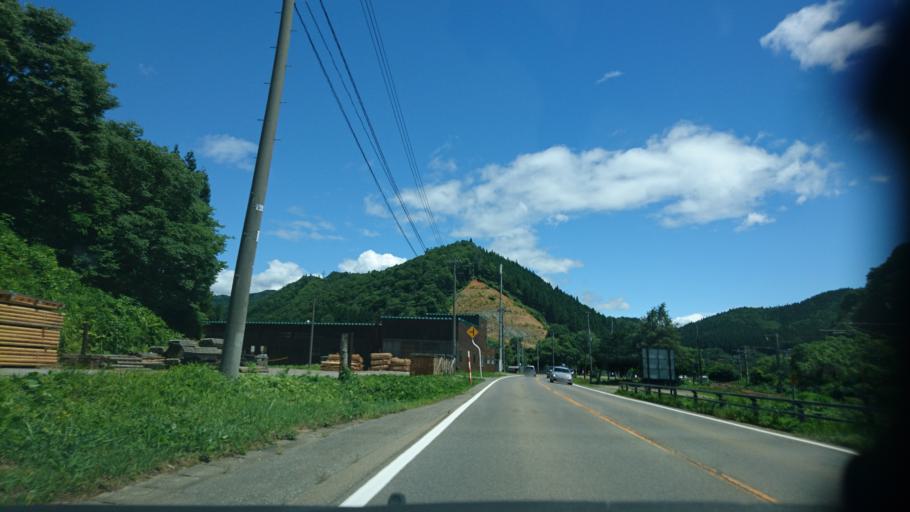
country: JP
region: Akita
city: Kakunodatemachi
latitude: 39.6500
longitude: 140.6667
